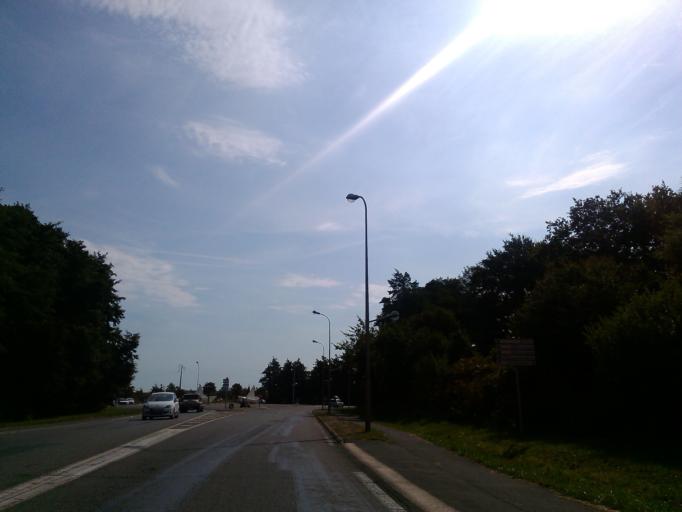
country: FR
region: Poitou-Charentes
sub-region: Departement de la Charente-Maritime
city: La Tremblade
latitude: 45.7854
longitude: -1.1587
